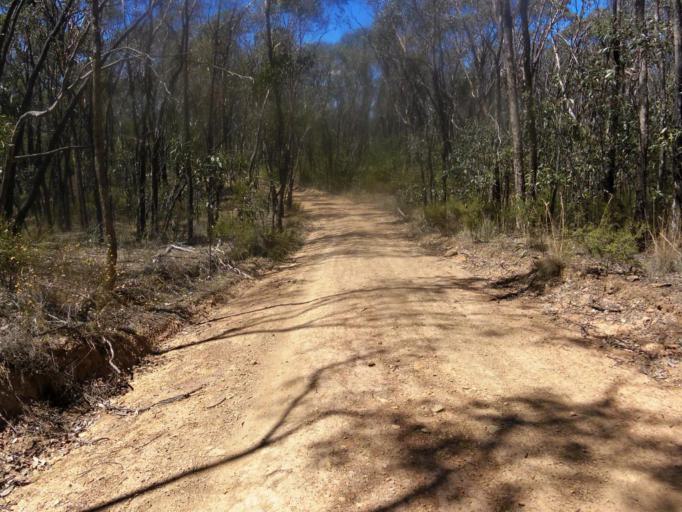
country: AU
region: Victoria
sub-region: Mount Alexander
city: Castlemaine
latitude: -37.0070
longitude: 144.1199
